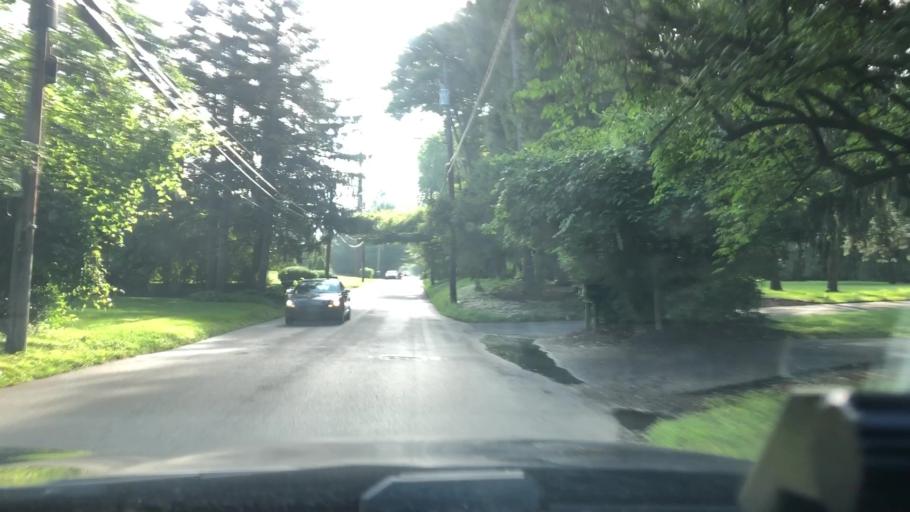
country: US
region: Pennsylvania
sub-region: Northampton County
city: Bethlehem
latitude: 40.6549
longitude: -75.3738
